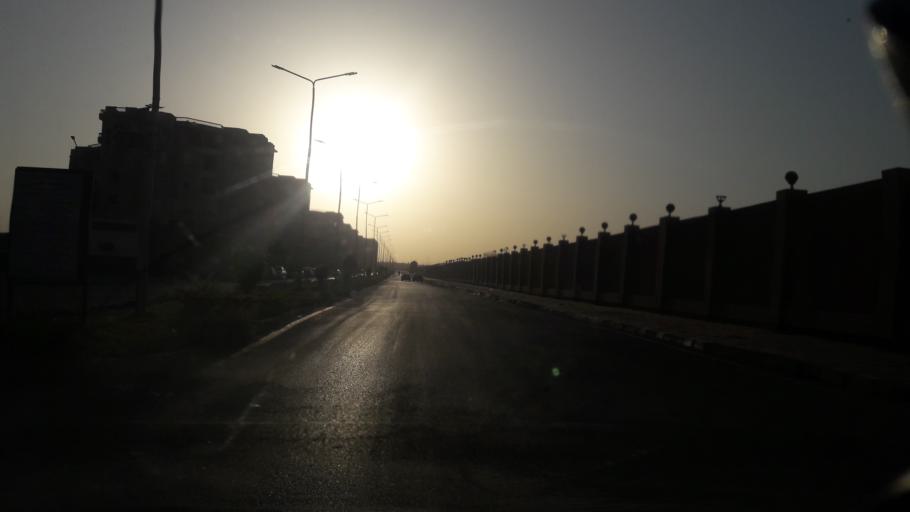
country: EG
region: Al Jizah
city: Madinat Sittah Uktubar
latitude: 29.9576
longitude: 31.0457
